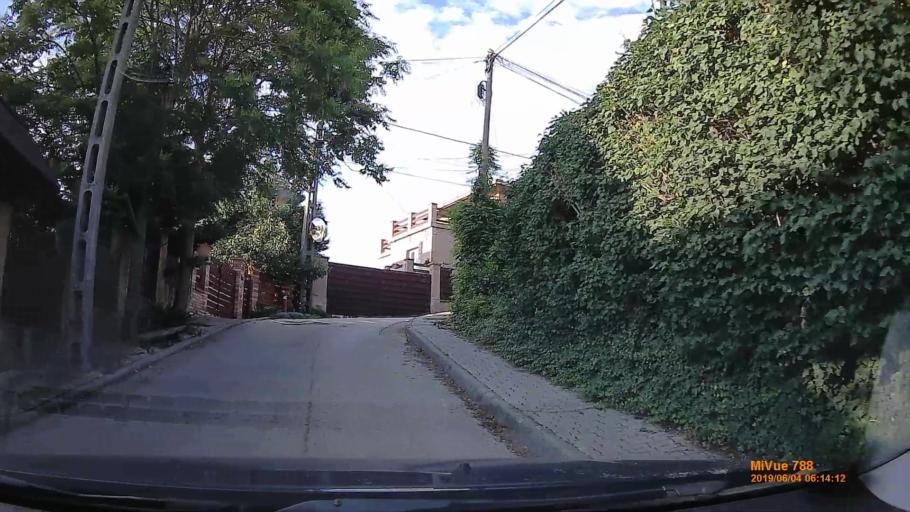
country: HU
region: Budapest
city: Budapest XXII. keruelet
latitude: 47.4341
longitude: 19.0316
